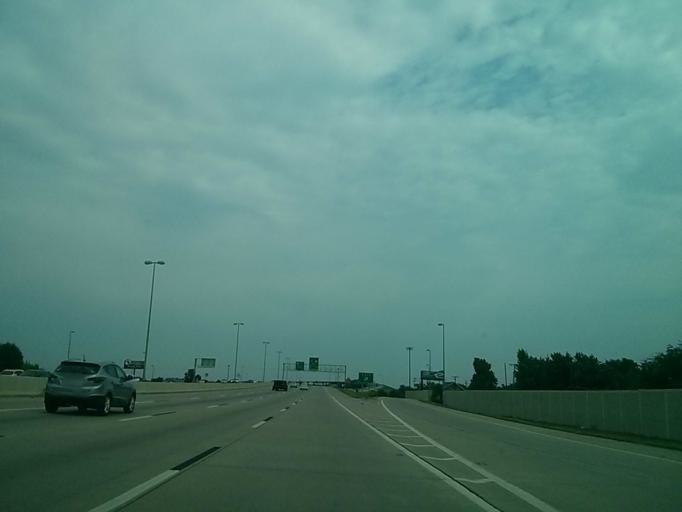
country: US
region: Oklahoma
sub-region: Tulsa County
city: Owasso
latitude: 36.1573
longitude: -95.8606
